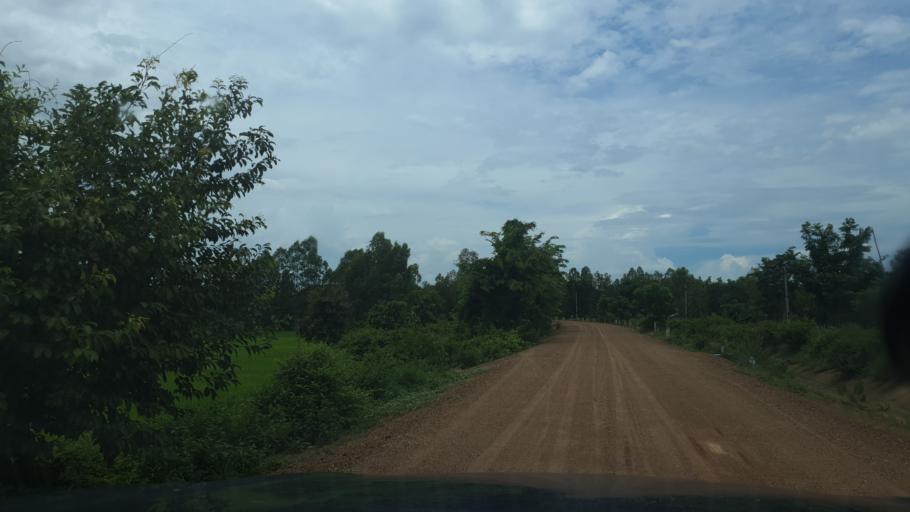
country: TH
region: Lampang
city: Hang Chat
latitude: 18.2830
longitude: 99.3721
